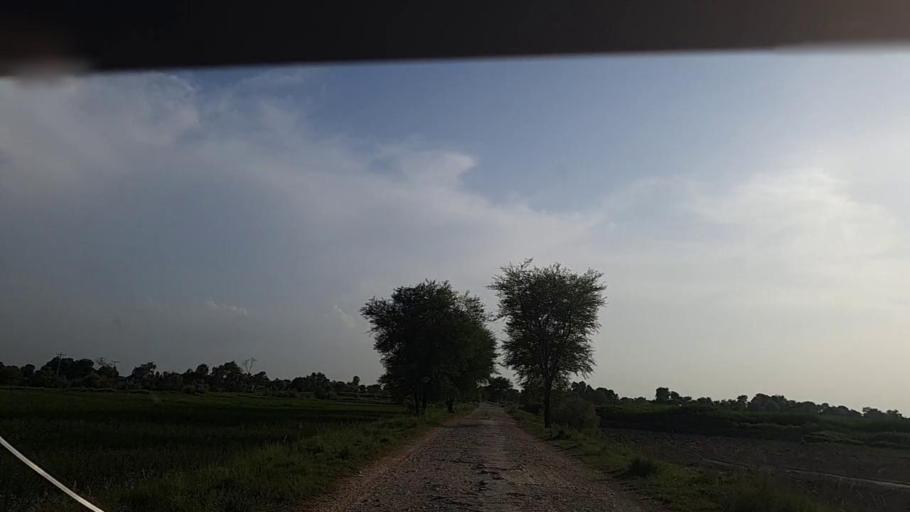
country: PK
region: Sindh
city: Khanpur
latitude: 27.8229
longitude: 69.3423
